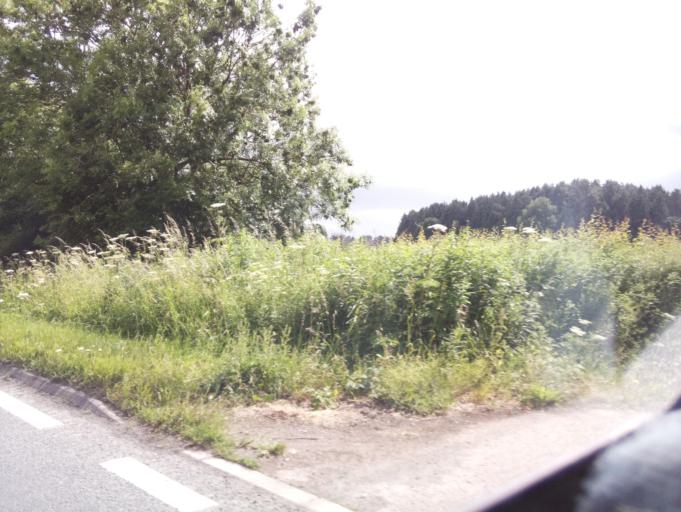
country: GB
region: England
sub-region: Derbyshire
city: Shirley
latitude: 52.9911
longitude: -1.6884
